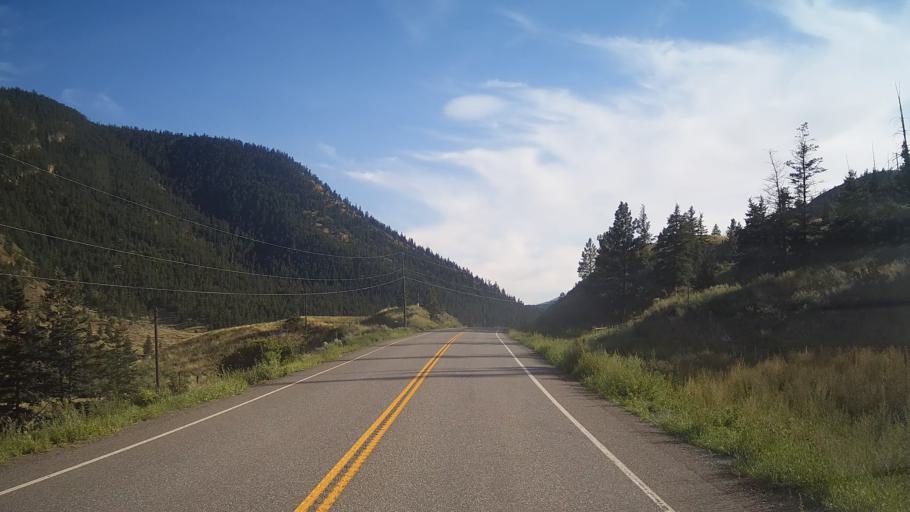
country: CA
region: British Columbia
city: Cache Creek
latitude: 50.8802
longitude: -121.5093
